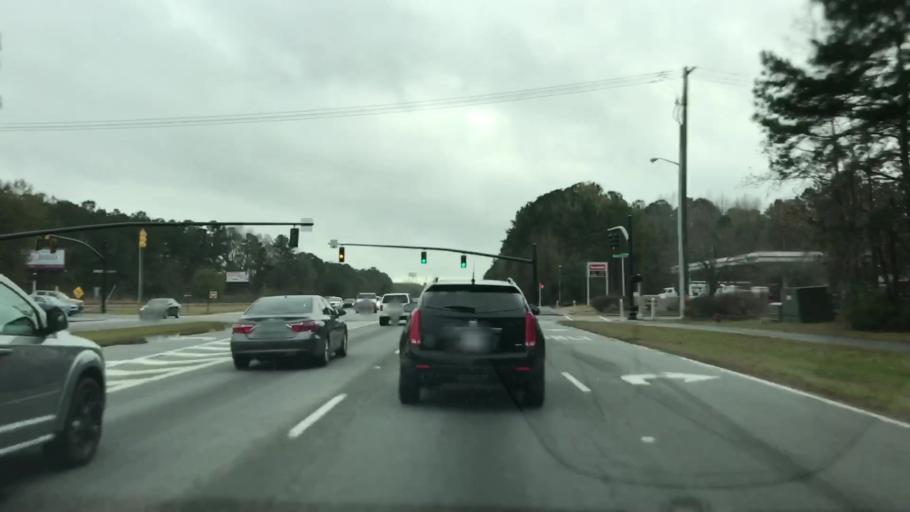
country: US
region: South Carolina
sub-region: Berkeley County
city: Goose Creek
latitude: 33.0189
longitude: -80.0361
